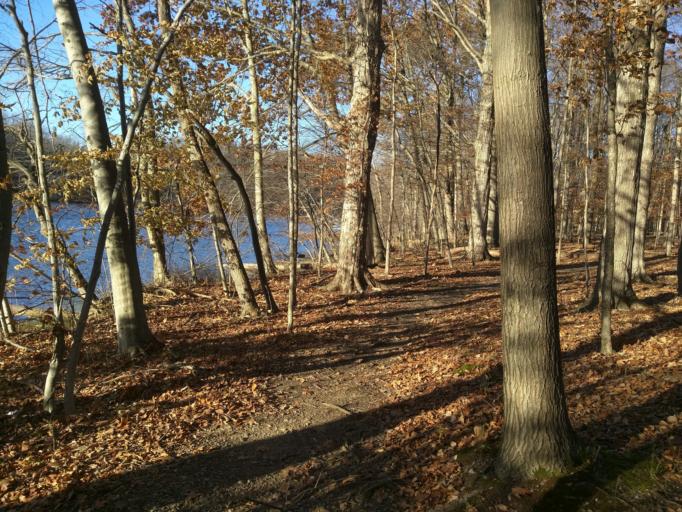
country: US
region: Michigan
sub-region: Eaton County
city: Waverly
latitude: 42.6962
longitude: -84.6139
